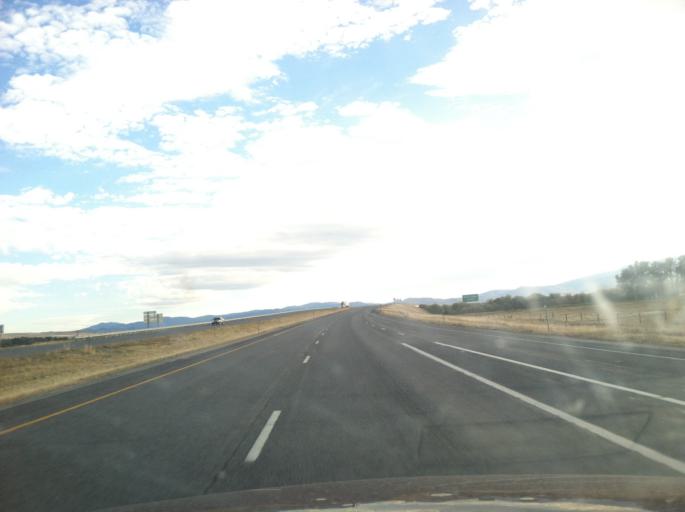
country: US
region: Montana
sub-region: Deer Lodge County
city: Warm Springs
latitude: 46.2701
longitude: -112.7485
